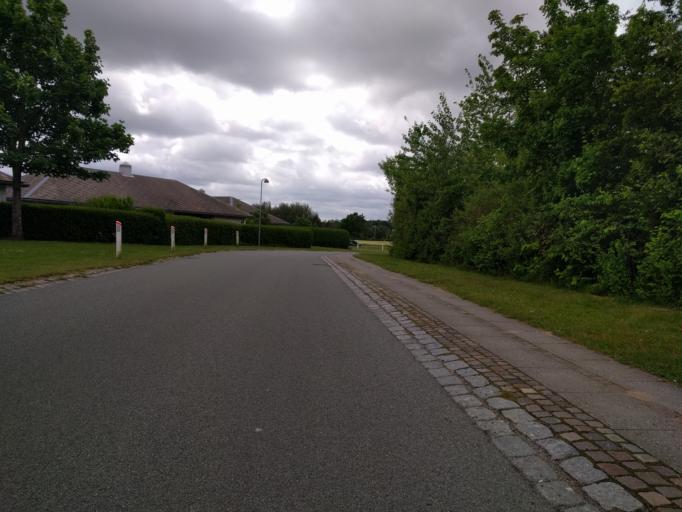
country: DK
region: South Denmark
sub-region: Odense Kommune
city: Seden
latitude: 55.4206
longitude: 10.4473
